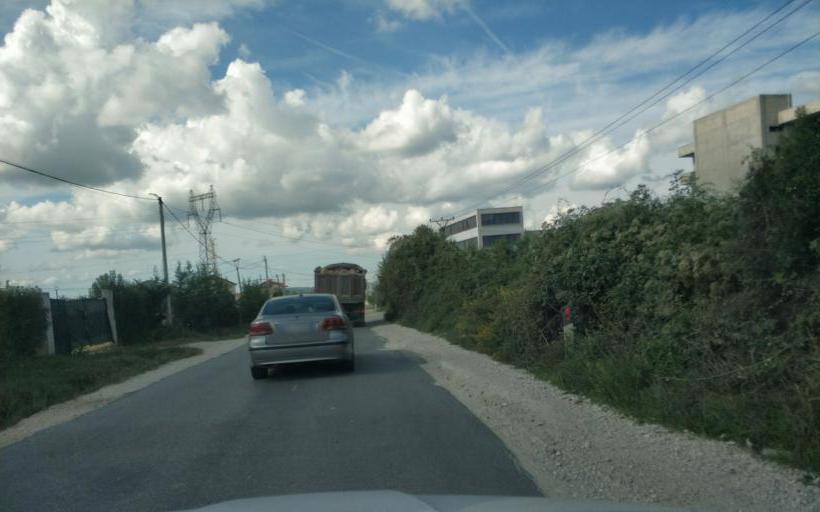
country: AL
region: Durres
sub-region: Rrethi i Krujes
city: Fushe-Kruje
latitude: 41.4767
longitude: 19.7453
